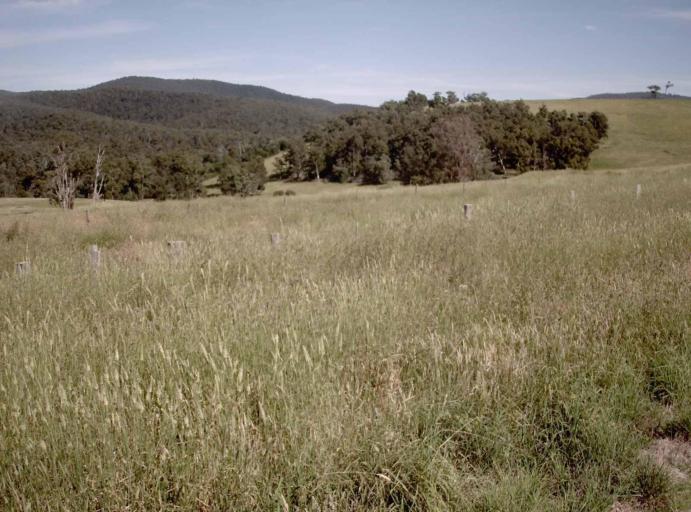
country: AU
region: Victoria
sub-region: East Gippsland
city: Lakes Entrance
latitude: -37.5000
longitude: 148.1328
